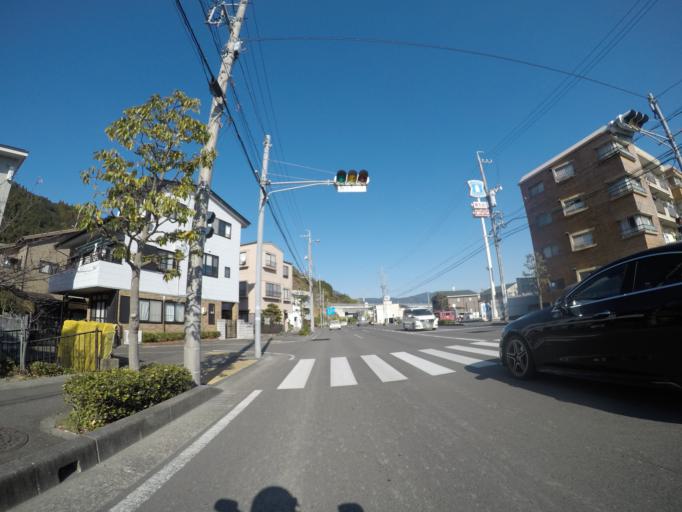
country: JP
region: Shizuoka
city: Shizuoka-shi
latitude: 35.0012
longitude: 138.3806
